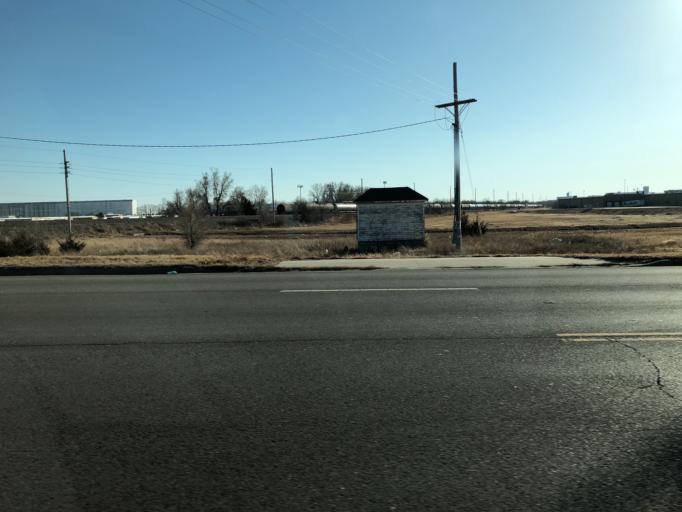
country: US
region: Kansas
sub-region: Reno County
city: Hutchinson
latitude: 38.0723
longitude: -97.8898
